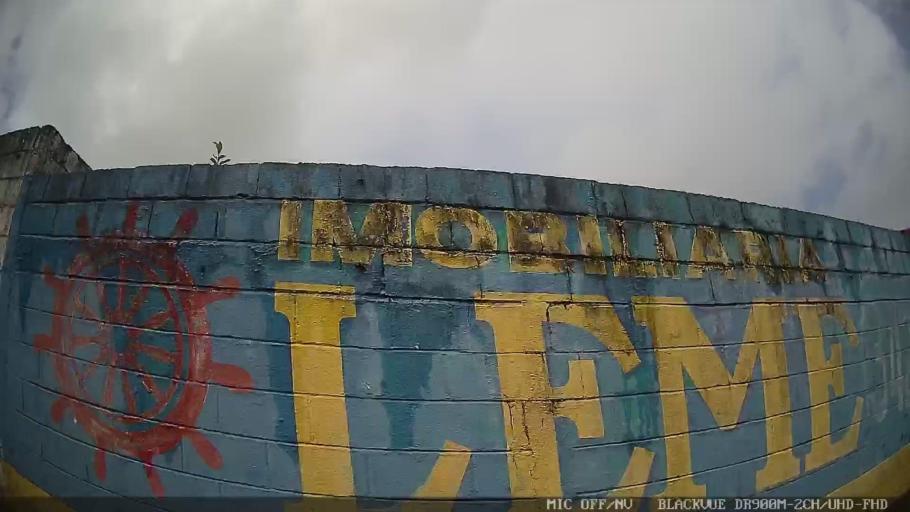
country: BR
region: Sao Paulo
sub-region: Itanhaem
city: Itanhaem
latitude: -24.2056
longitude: -46.8332
